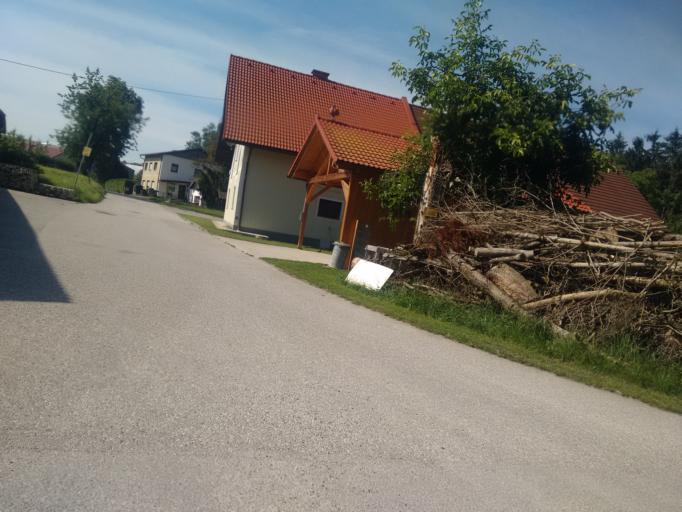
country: AT
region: Upper Austria
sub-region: Politischer Bezirk Grieskirchen
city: Bad Schallerbach
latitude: 48.1944
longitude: 13.9429
